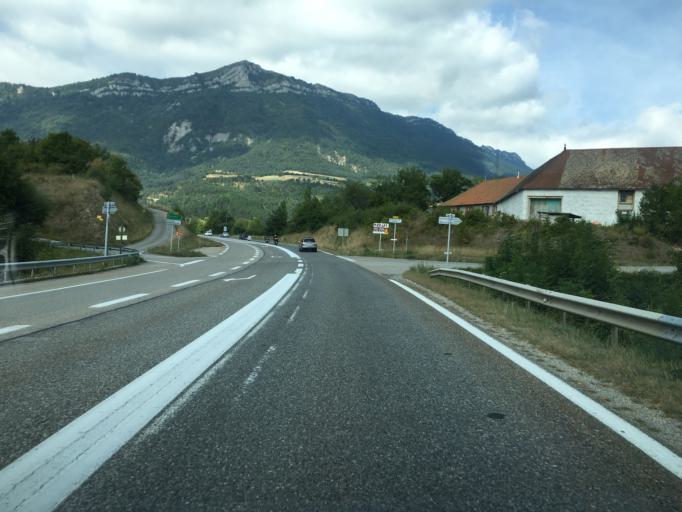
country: FR
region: Rhone-Alpes
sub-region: Departement de l'Isere
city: Mens
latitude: 44.7874
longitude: 5.6443
